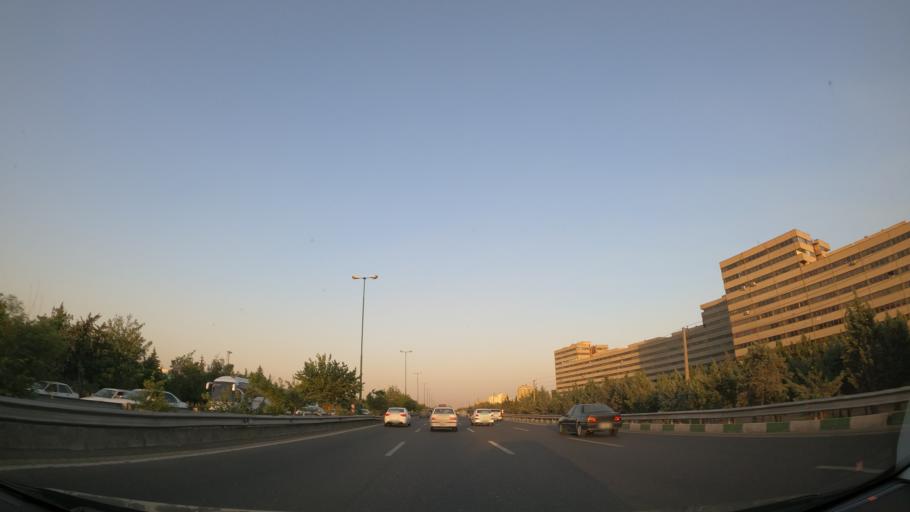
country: IR
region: Tehran
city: Tehran
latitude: 35.7161
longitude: 51.3171
